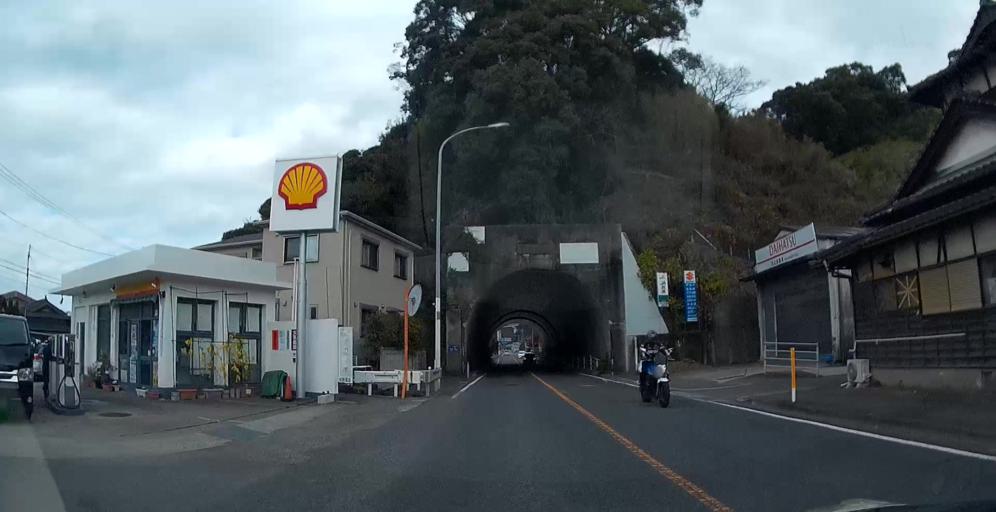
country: JP
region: Kumamoto
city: Minamata
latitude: 32.3485
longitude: 130.5040
